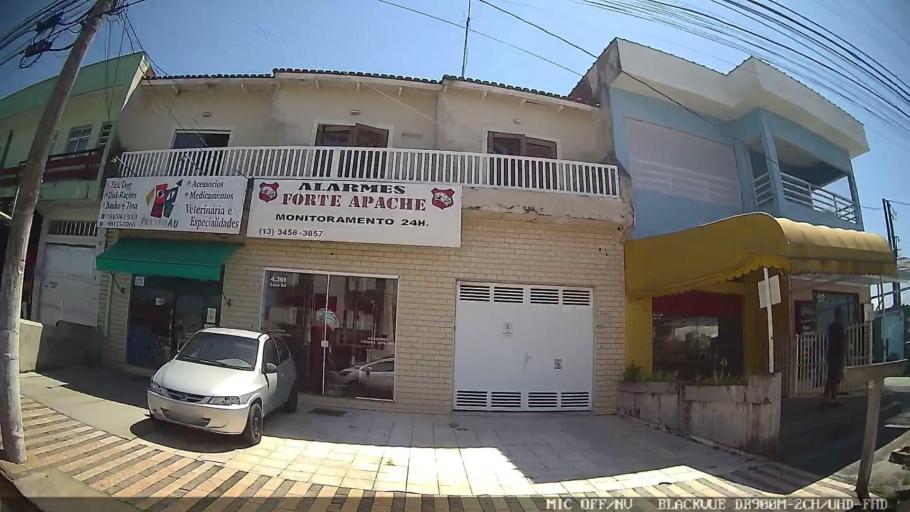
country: BR
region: Sao Paulo
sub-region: Peruibe
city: Peruibe
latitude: -24.3006
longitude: -46.9738
